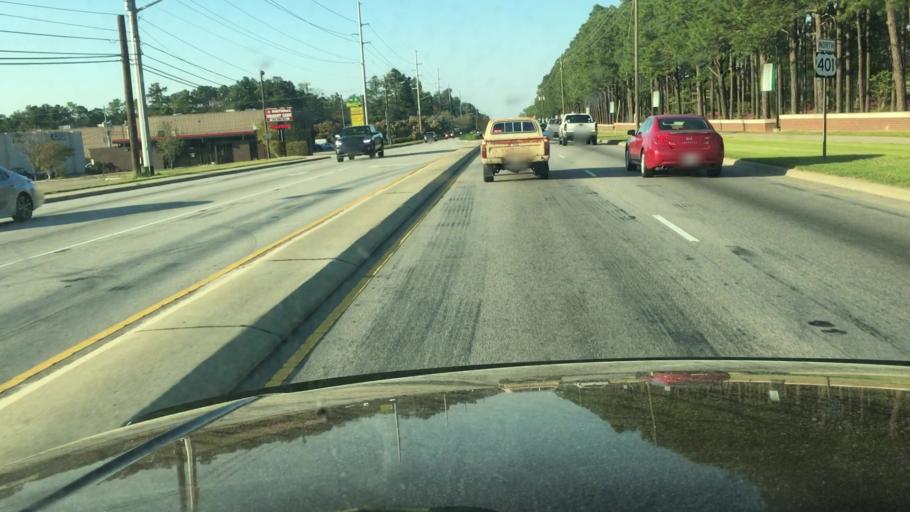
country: US
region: North Carolina
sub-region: Cumberland County
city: Fayetteville
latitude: 35.1324
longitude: -78.8774
